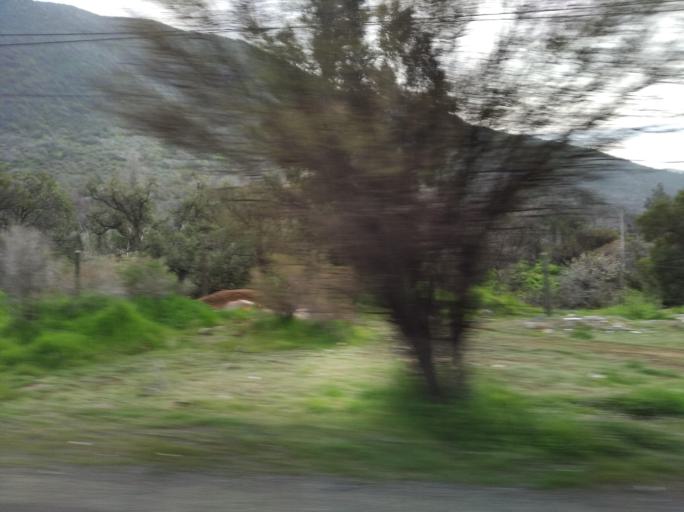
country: CL
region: Santiago Metropolitan
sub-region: Provincia de Chacabuco
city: Lampa
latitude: -33.0774
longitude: -70.9477
